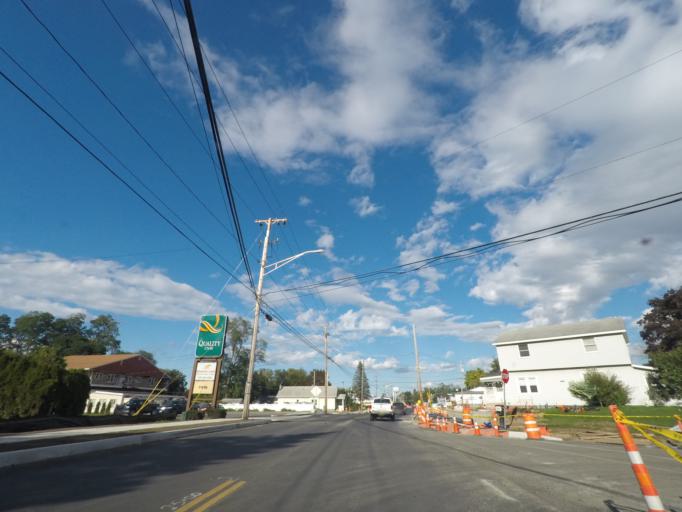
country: US
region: New York
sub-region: Schenectady County
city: Rotterdam
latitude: 42.7721
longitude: -73.9367
